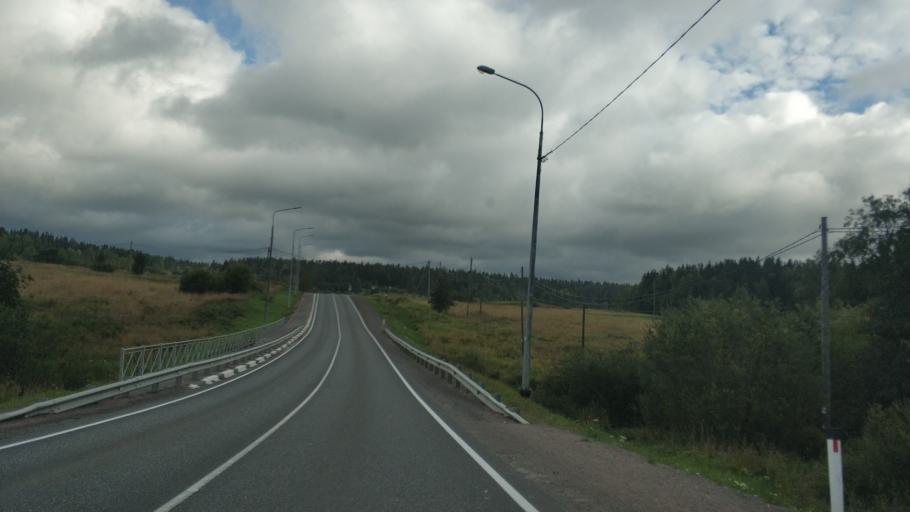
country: RU
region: Republic of Karelia
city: Khelyulya
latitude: 61.7575
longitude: 30.6571
